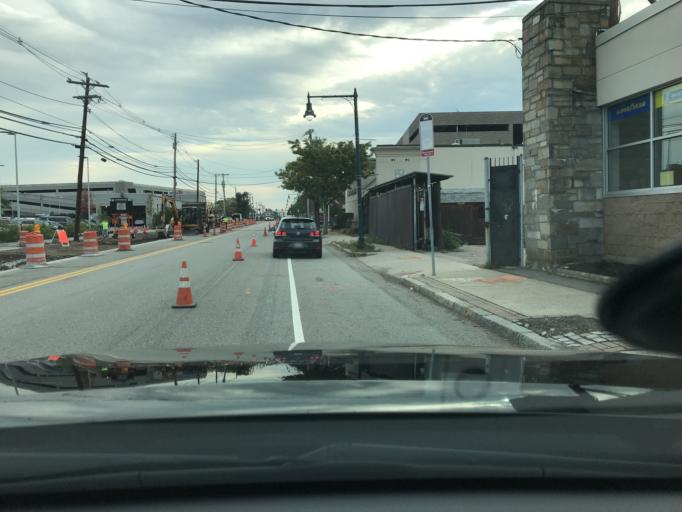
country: US
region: Massachusetts
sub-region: Middlesex County
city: Watertown
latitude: 42.3641
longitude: -71.1710
